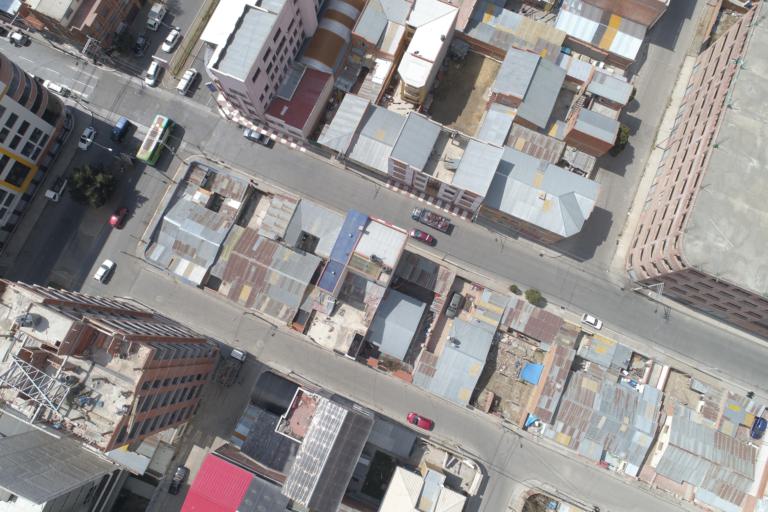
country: BO
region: La Paz
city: La Paz
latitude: -16.5281
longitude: -68.1491
